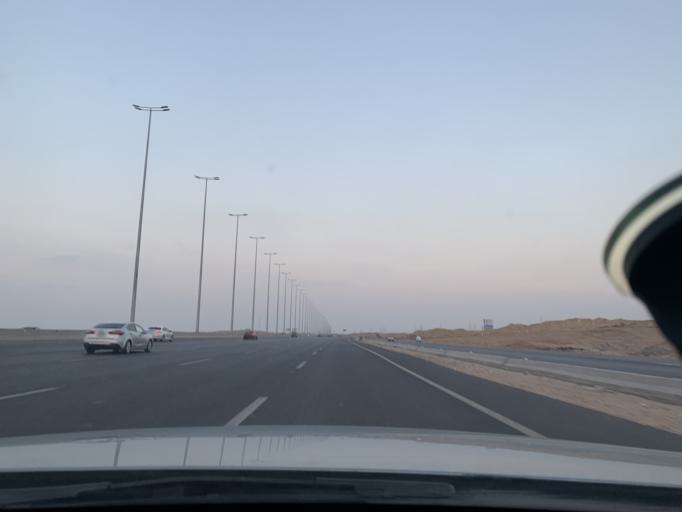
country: EG
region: Muhafazat al Qalyubiyah
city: Al Khankah
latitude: 30.0895
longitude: 31.5102
